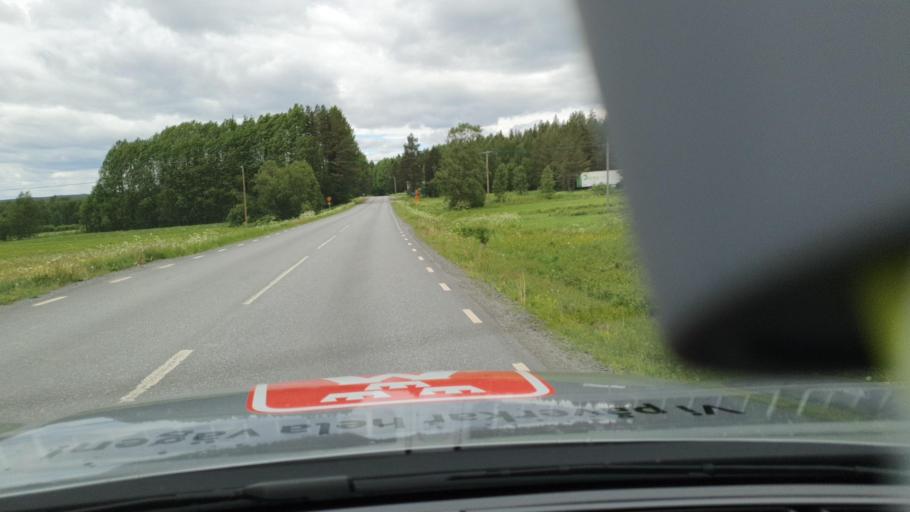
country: SE
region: Norrbotten
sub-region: Lulea Kommun
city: Sodra Sunderbyn
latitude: 65.8277
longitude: 21.9718
